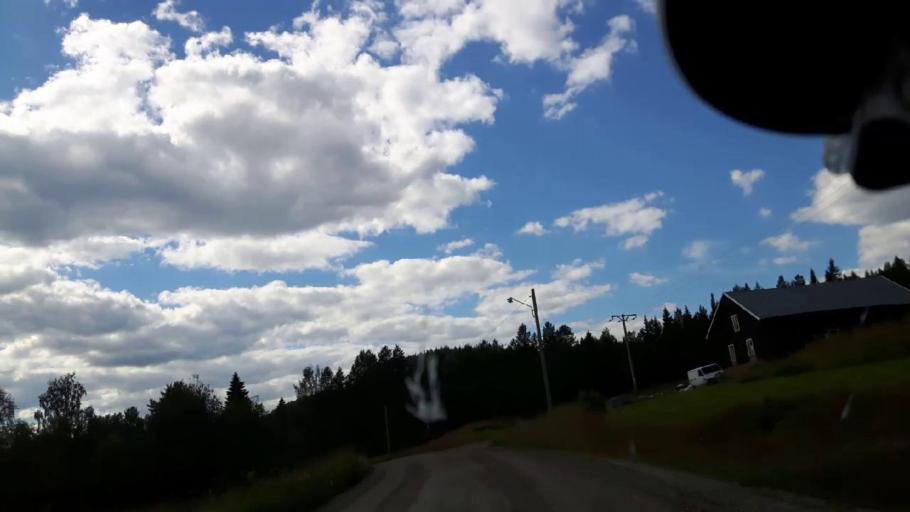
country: SE
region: Jaemtland
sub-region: Braecke Kommun
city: Braecke
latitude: 62.7198
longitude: 15.5835
